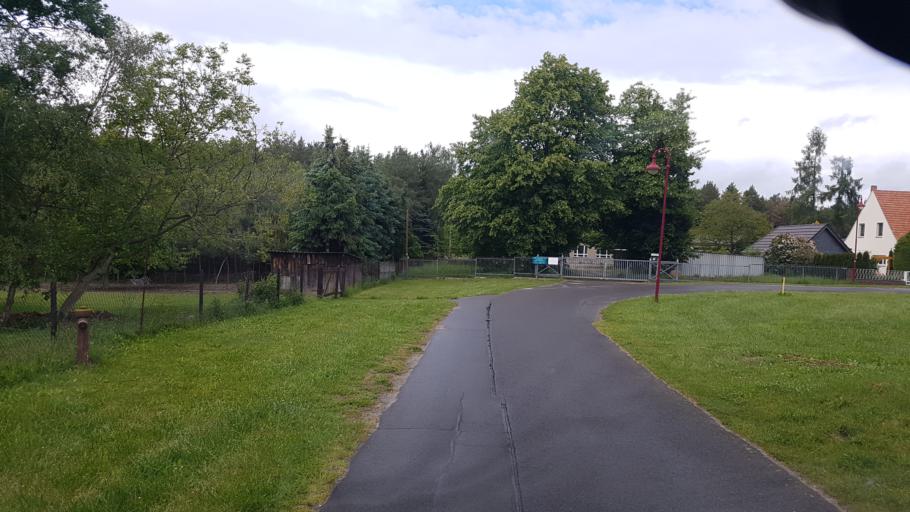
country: DE
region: Brandenburg
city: Hohenleipisch
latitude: 51.5001
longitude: 13.5664
